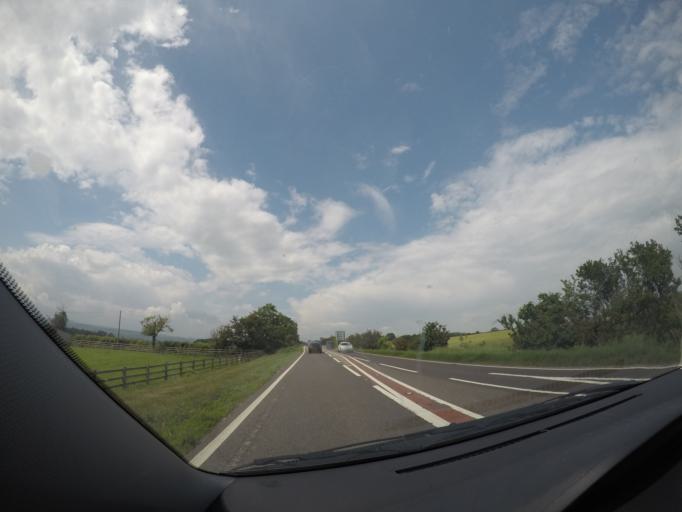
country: GB
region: England
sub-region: County Durham
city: Hutton Magna
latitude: 54.4737
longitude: -1.7627
